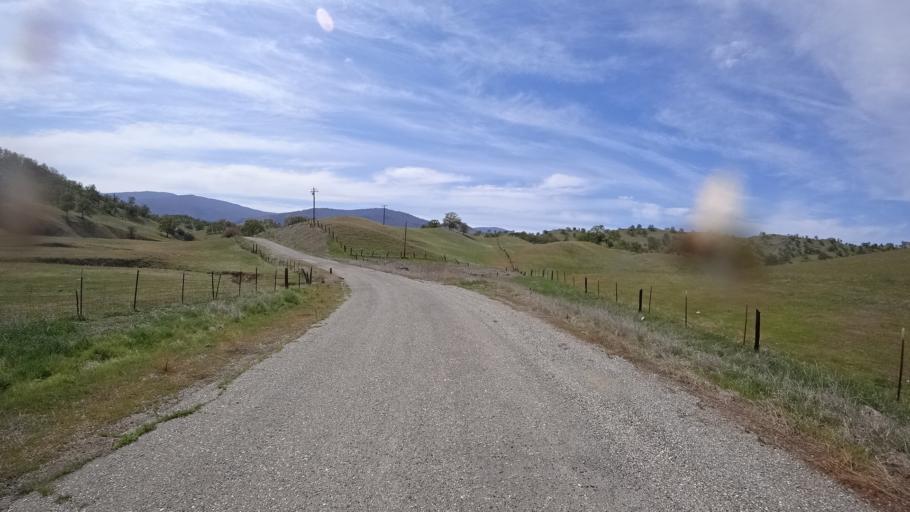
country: US
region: California
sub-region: Glenn County
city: Willows
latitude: 39.6138
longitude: -122.5726
